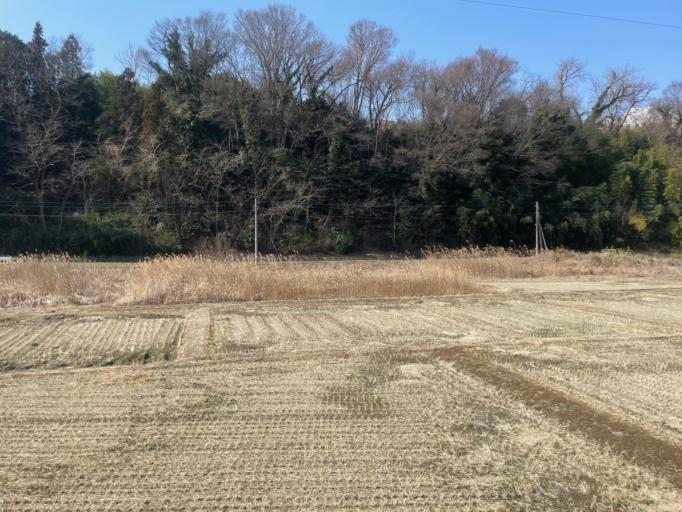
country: JP
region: Gunma
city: Shibukawa
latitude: 36.5215
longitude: 138.9907
